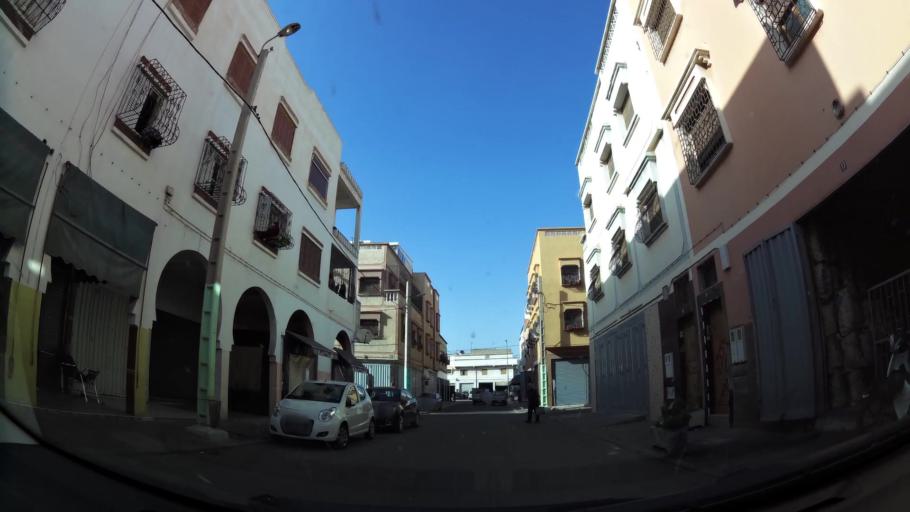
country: MA
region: Souss-Massa-Draa
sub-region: Inezgane-Ait Mellou
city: Inezgane
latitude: 30.3713
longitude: -9.5310
